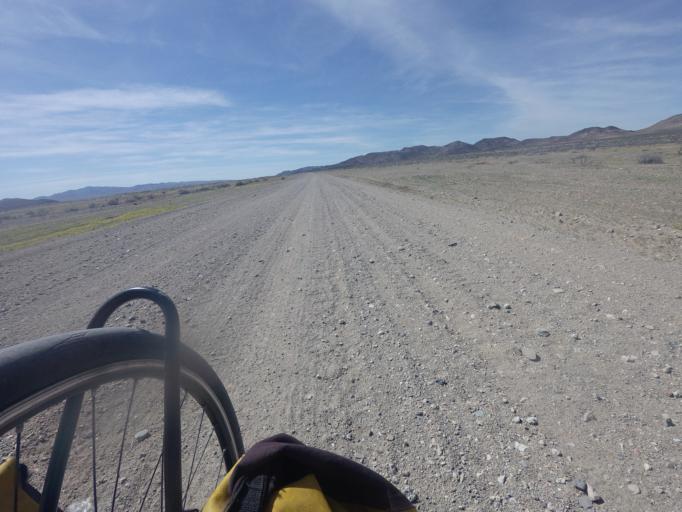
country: US
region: California
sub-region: San Bernardino County
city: Searles Valley
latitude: 35.5939
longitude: -117.4100
